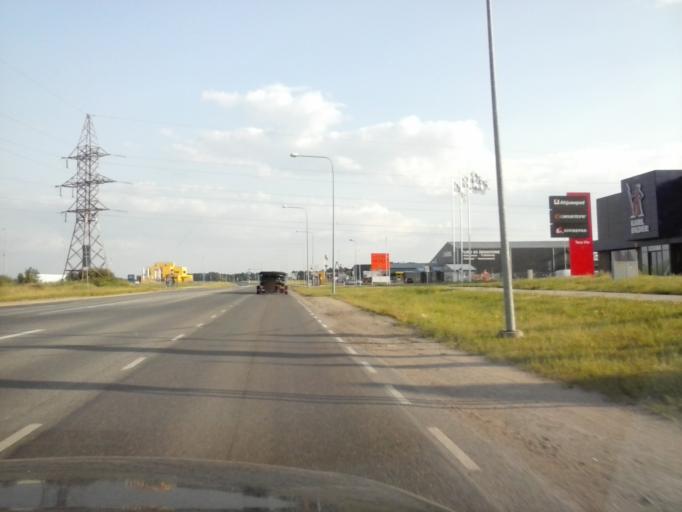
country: EE
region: Tartu
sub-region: UElenurme vald
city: Ulenurme
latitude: 58.3464
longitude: 26.7411
